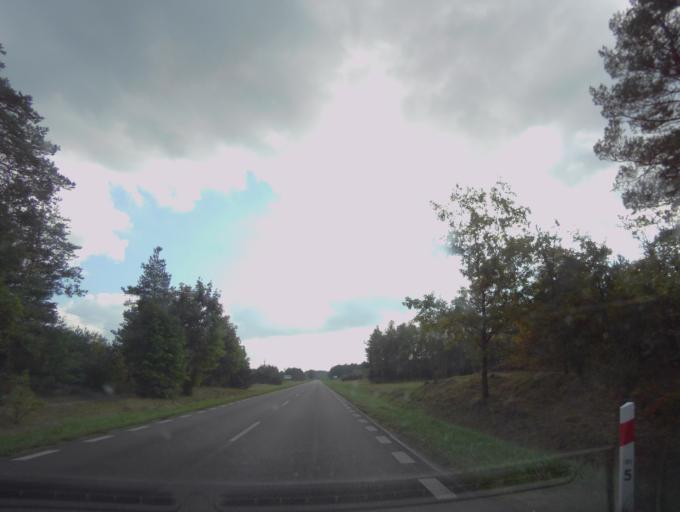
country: PL
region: Lublin Voivodeship
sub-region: Powiat bilgorajski
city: Bilgoraj
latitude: 50.5857
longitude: 22.6836
